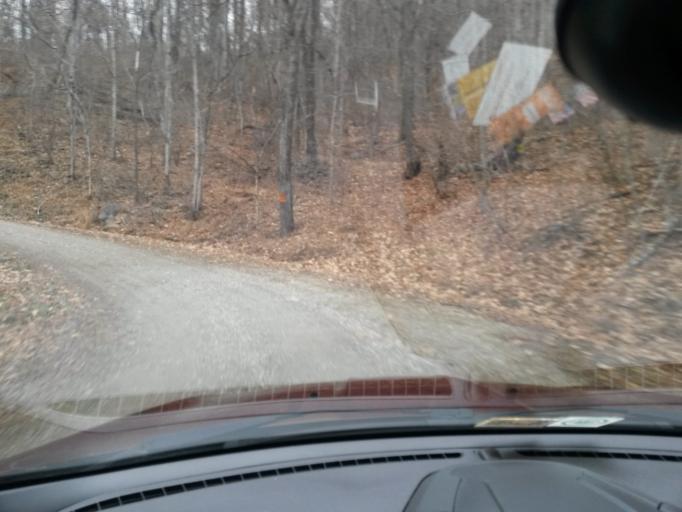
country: US
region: Virginia
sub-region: City of Buena Vista
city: Buena Vista
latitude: 37.7161
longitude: -79.2410
